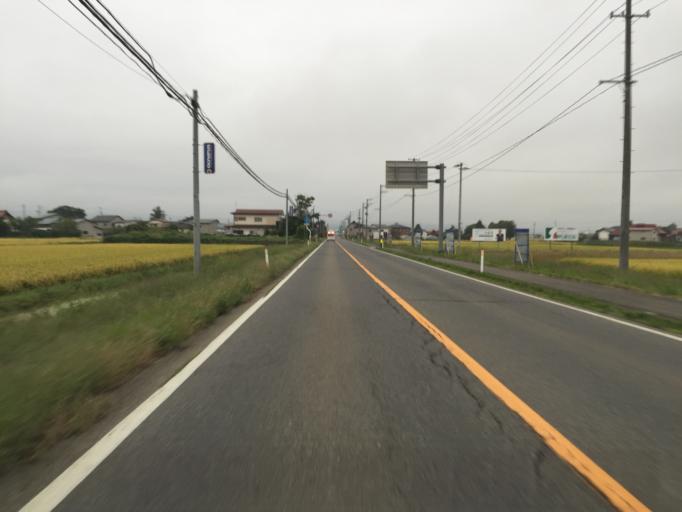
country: JP
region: Fukushima
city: Kitakata
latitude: 37.5247
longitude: 139.8914
